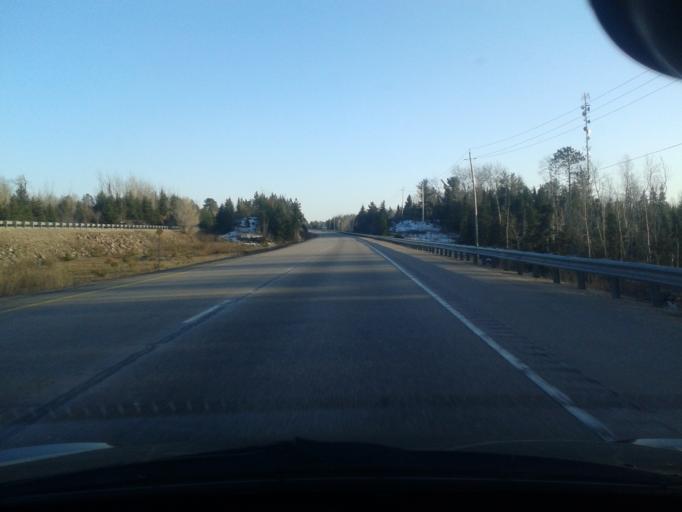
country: CA
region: Ontario
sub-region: Nipissing District
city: North Bay
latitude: 46.2290
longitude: -79.3499
